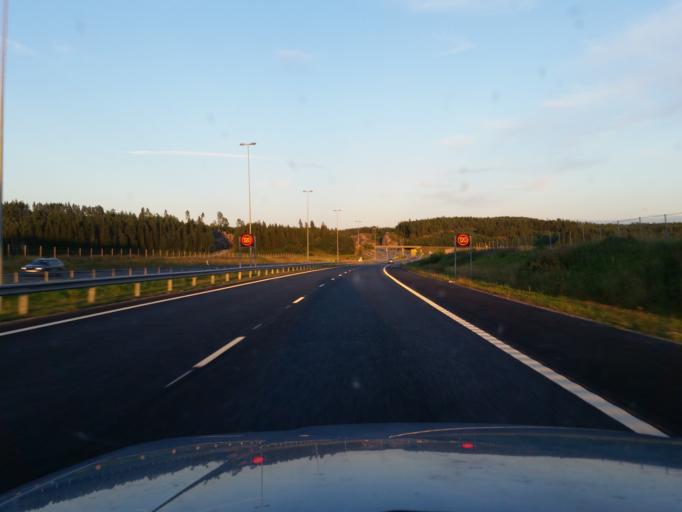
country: FI
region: Varsinais-Suomi
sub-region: Salo
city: Muurla
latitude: 60.3854
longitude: 23.3060
